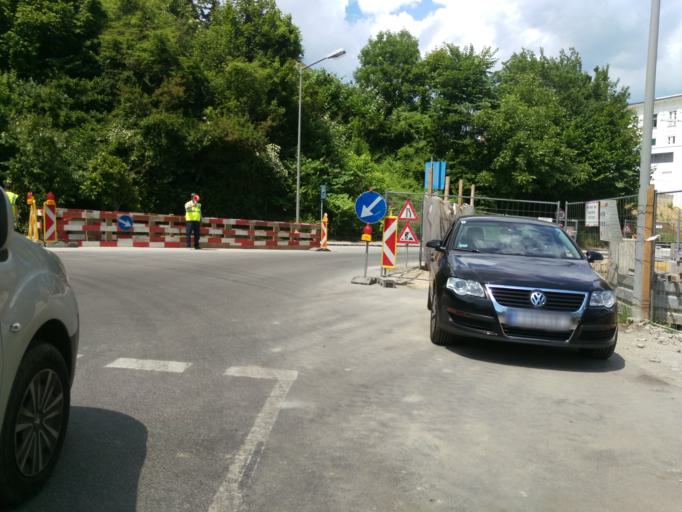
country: AT
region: Styria
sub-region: Graz Stadt
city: Graz
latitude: 47.0822
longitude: 15.4684
